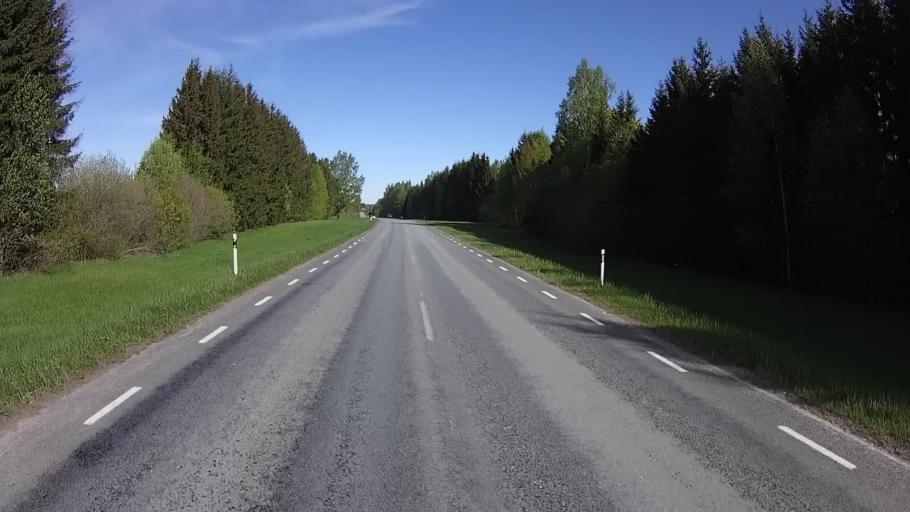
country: EE
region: Polvamaa
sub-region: Polva linn
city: Polva
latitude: 58.2325
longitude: 27.0213
